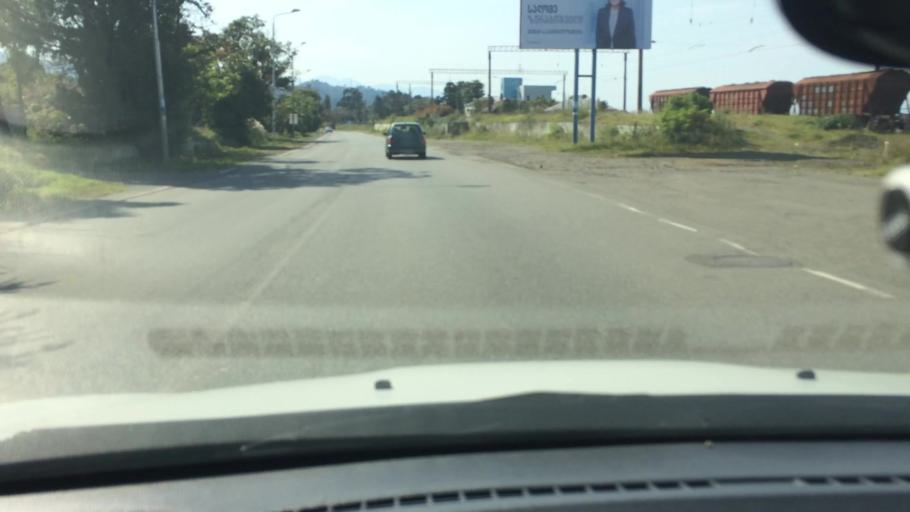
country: GE
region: Ajaria
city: Makhinjauri
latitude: 41.7328
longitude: 41.7324
